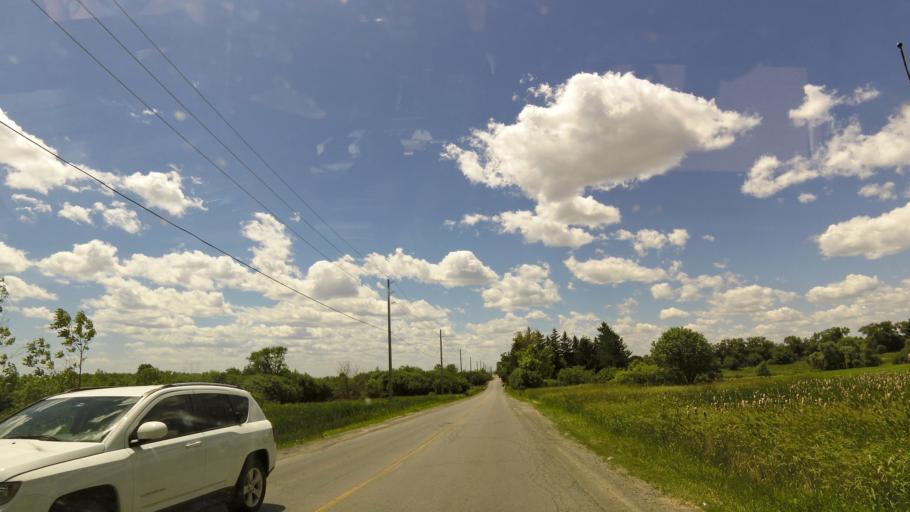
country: CA
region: Ontario
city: Oshawa
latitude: 43.9591
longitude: -78.8475
